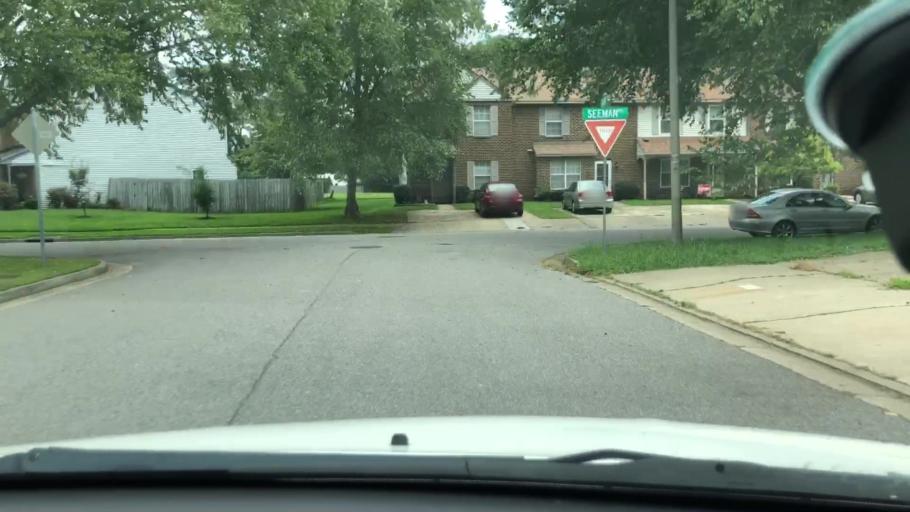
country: US
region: Virginia
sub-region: City of Virginia Beach
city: Virginia Beach
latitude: 36.8430
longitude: -76.1120
